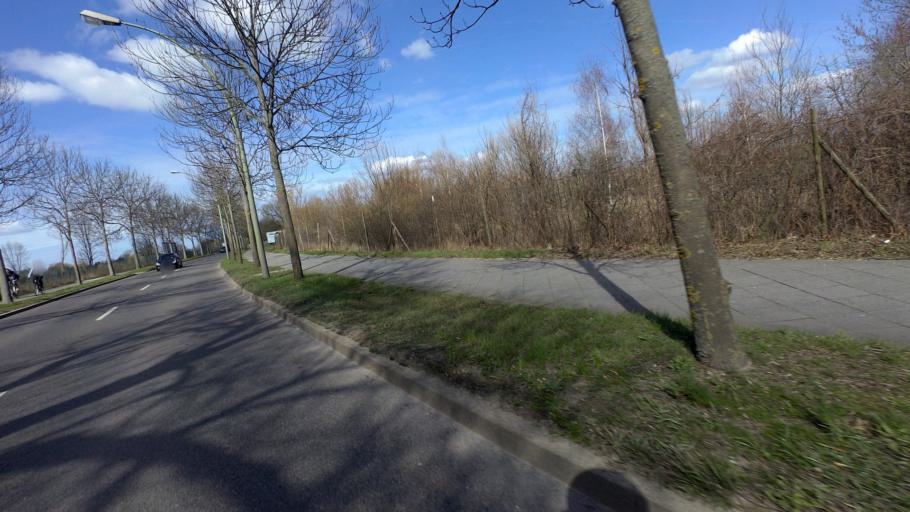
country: DE
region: Berlin
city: Blankenburg
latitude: 52.5852
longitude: 13.4600
